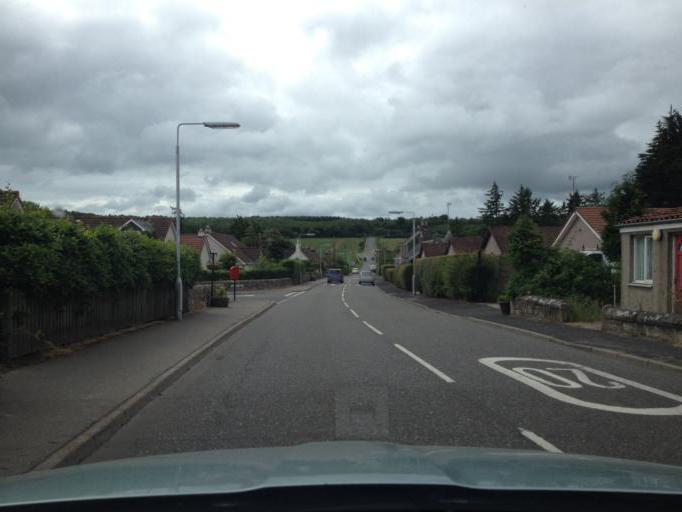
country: GB
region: Scotland
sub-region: Fife
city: Strathkinness
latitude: 56.3327
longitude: -2.8765
